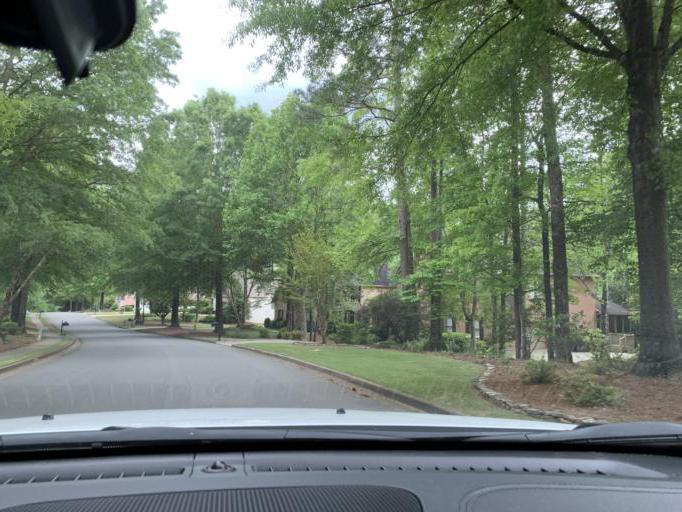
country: US
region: Georgia
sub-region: Gwinnett County
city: Suwanee
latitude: 34.1113
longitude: -84.1126
